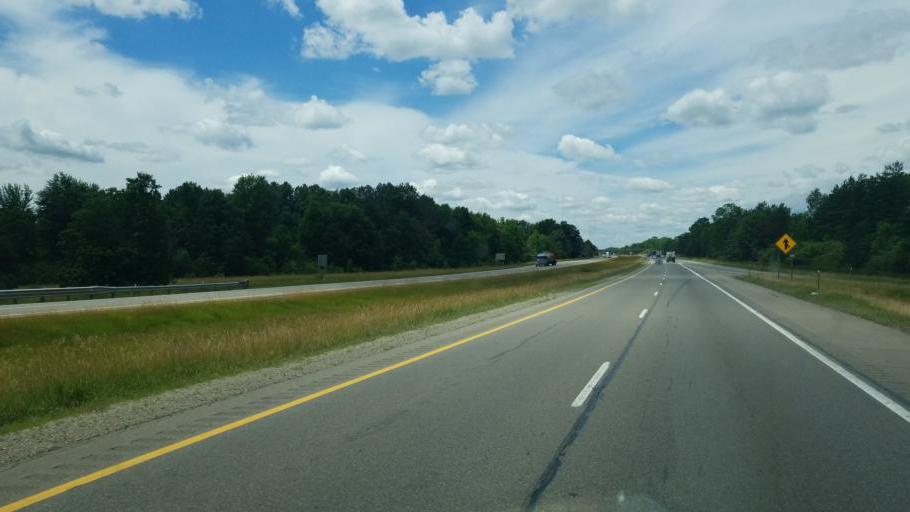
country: US
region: Michigan
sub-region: Eaton County
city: Dimondale
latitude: 42.6652
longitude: -84.5918
